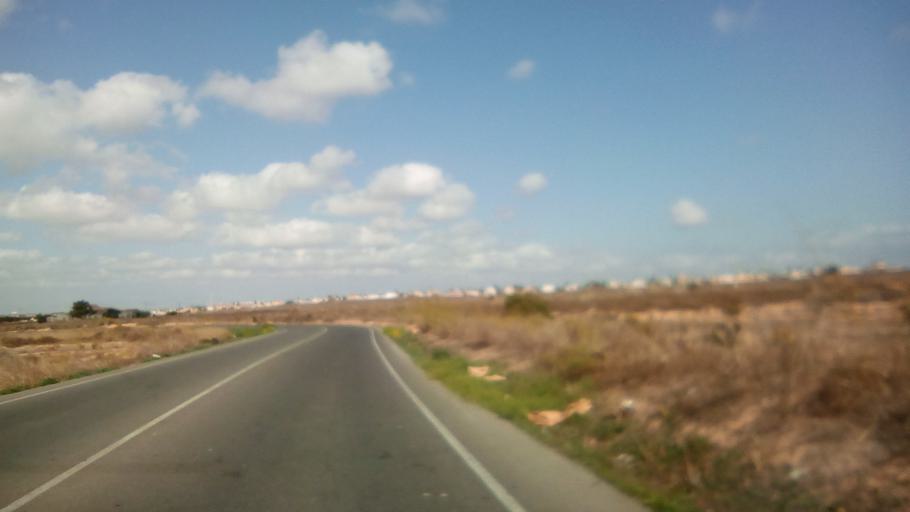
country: ES
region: Valencia
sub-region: Provincia de Alicante
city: Torrevieja
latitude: 37.9995
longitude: -0.6857
